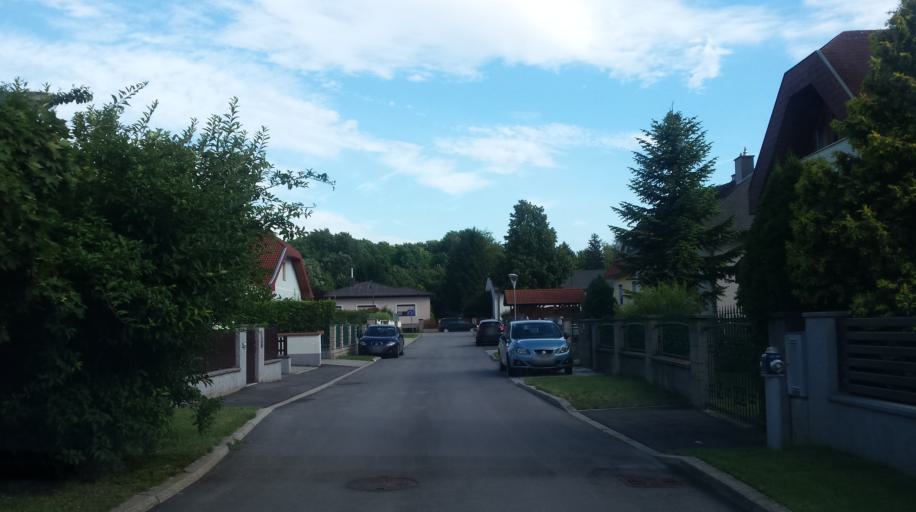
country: AT
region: Burgenland
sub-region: Eisenstadt-Umgebung
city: Leithaprodersdorf
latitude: 47.9441
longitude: 16.4812
